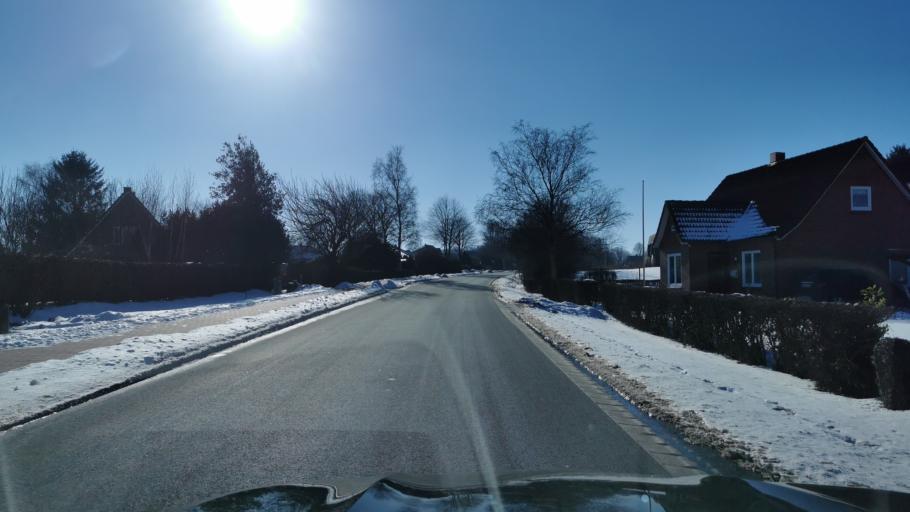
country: DE
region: Schleswig-Holstein
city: Grundhof
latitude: 54.7720
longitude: 9.6524
